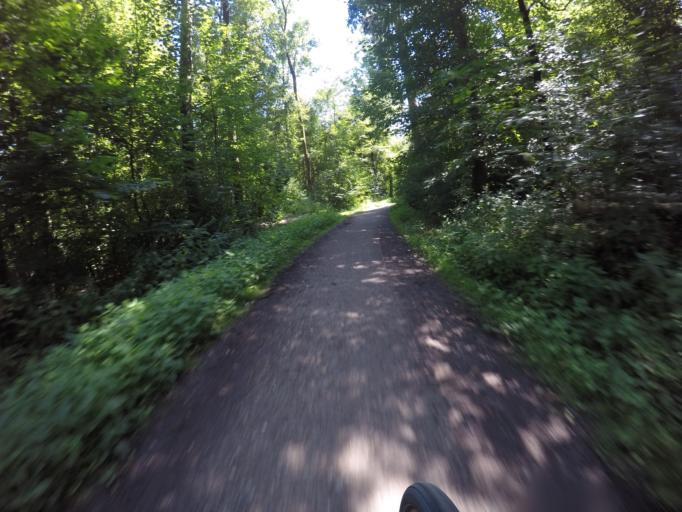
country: DE
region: Baden-Wuerttemberg
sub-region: Regierungsbezirk Stuttgart
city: Leinfelden-Echterdingen
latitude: 48.7156
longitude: 9.1691
